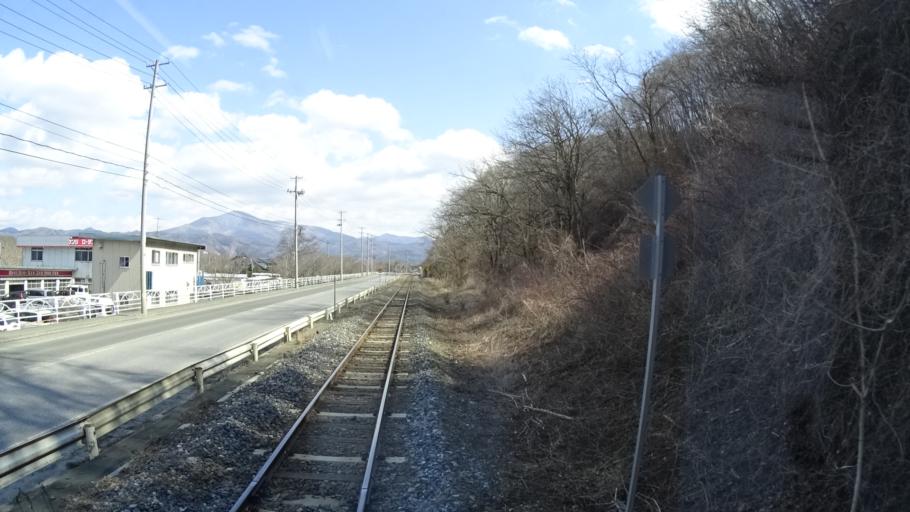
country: JP
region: Iwate
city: Tono
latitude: 39.3315
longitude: 141.5454
